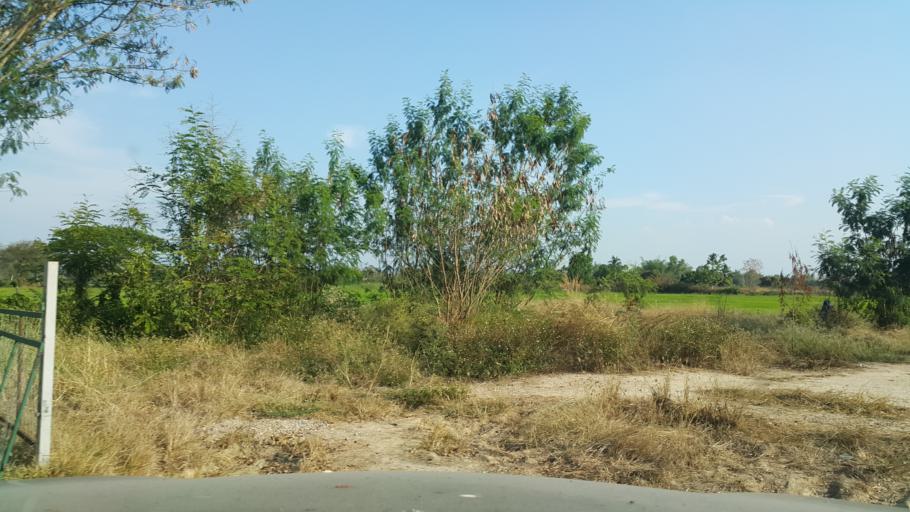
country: TH
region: Chiang Mai
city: San Sai
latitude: 18.8334
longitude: 99.0912
